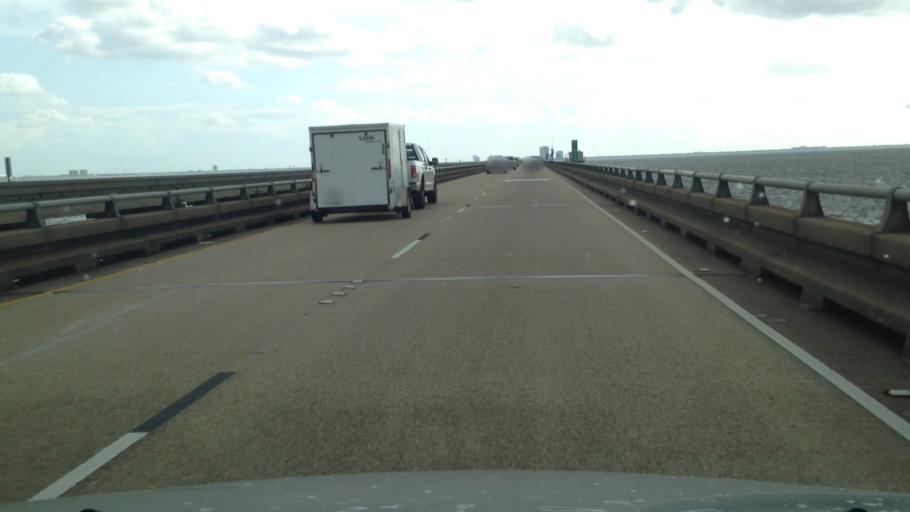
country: US
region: Louisiana
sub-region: Jefferson Parish
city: Metairie
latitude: 30.0927
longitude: -90.1417
